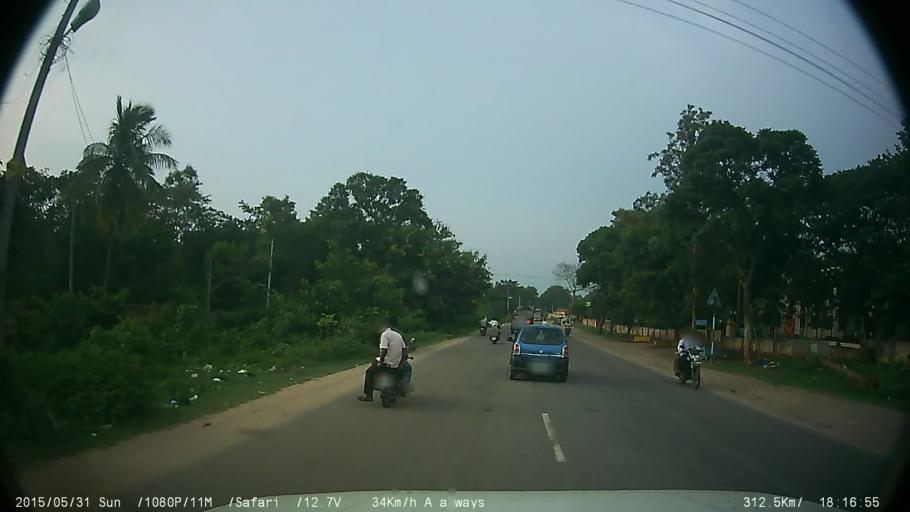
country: IN
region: Karnataka
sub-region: Mysore
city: Nanjangud
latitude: 12.1166
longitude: 76.6741
